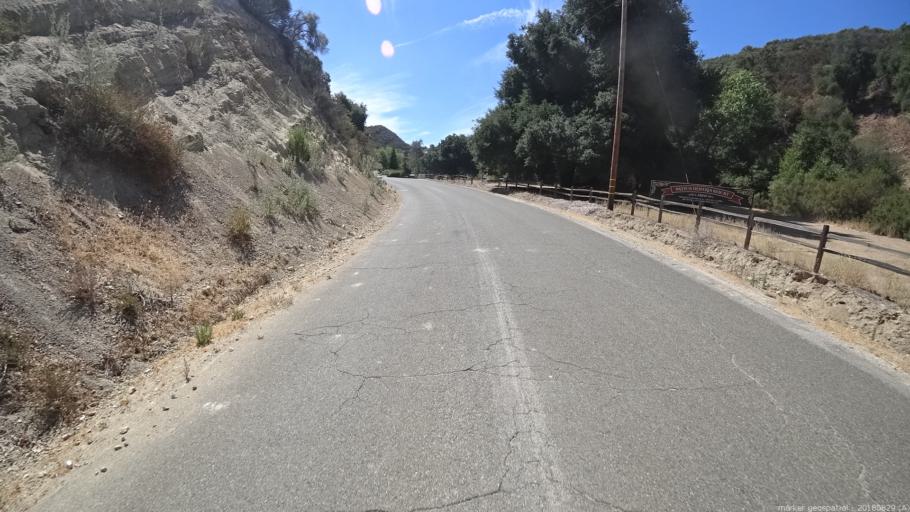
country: US
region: California
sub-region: San Luis Obispo County
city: Lake Nacimiento
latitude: 35.8312
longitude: -121.0501
